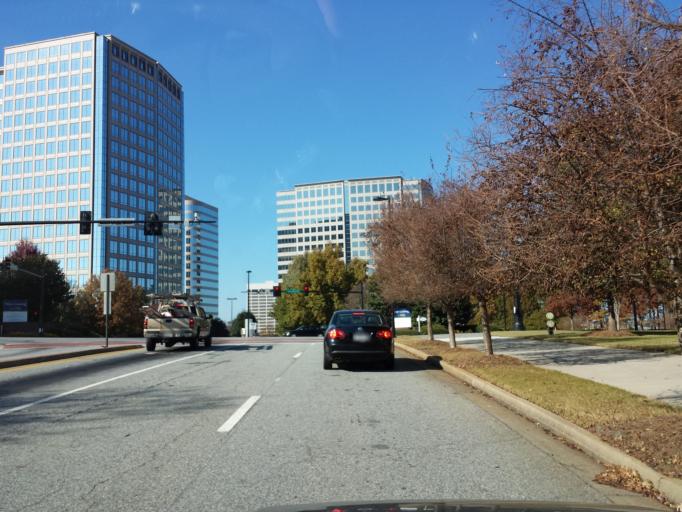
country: US
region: Georgia
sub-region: Cobb County
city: Vinings
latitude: 33.8845
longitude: -84.4597
